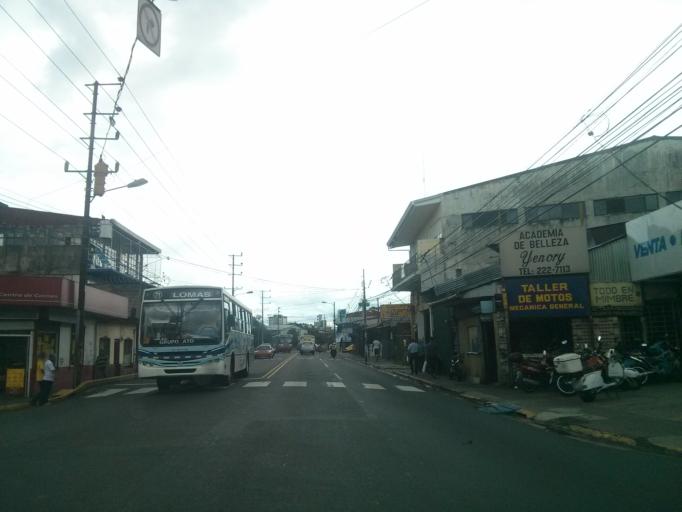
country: CR
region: San Jose
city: San Jose
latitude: 9.9224
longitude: -84.0729
